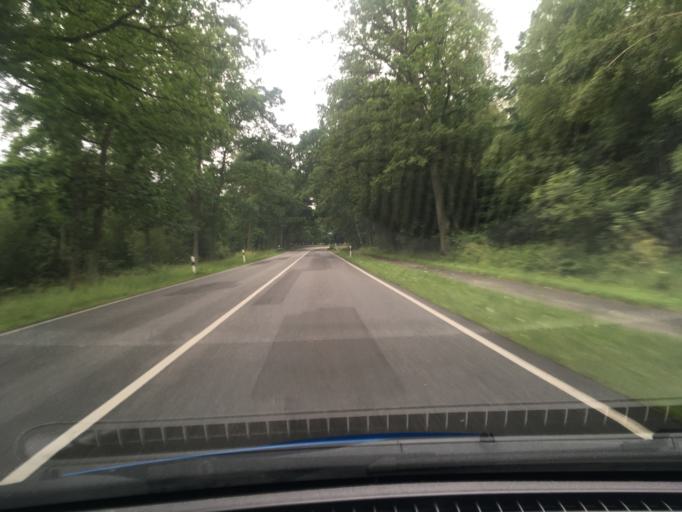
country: DE
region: Mecklenburg-Vorpommern
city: Stralendorf
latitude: 53.5464
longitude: 11.3183
